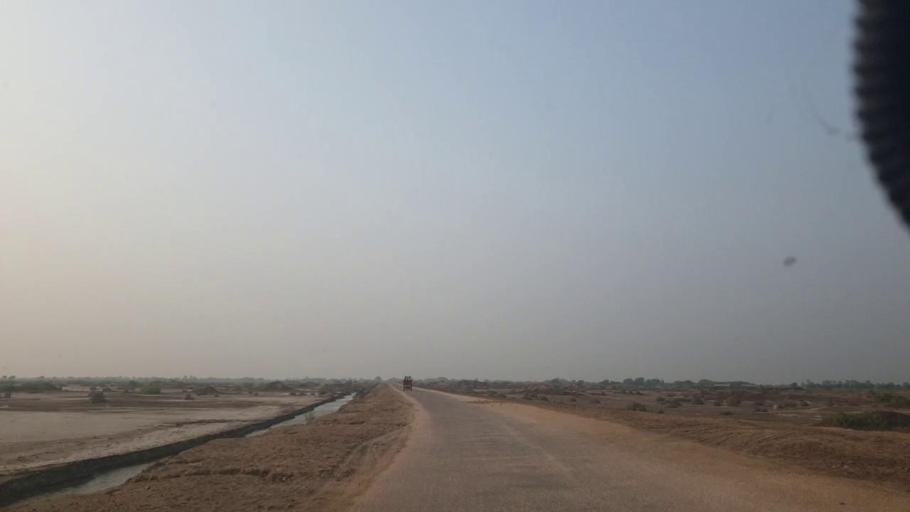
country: PK
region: Sindh
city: Bulri
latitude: 24.8533
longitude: 68.4042
